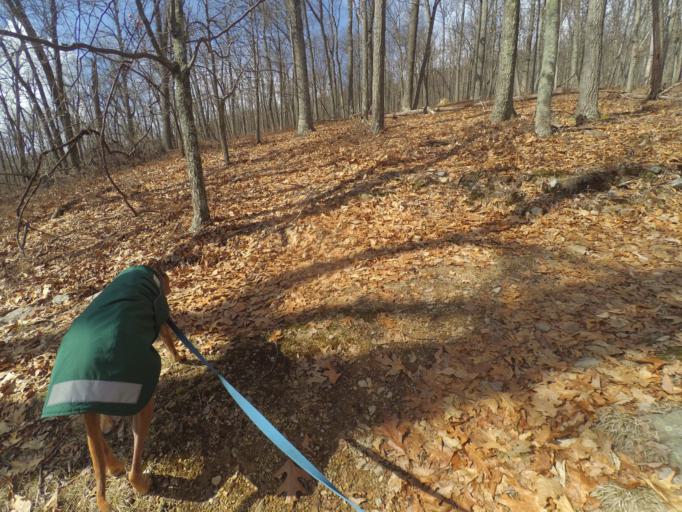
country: US
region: Pennsylvania
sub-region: Centre County
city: Centre Hall
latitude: 40.7653
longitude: -77.7034
